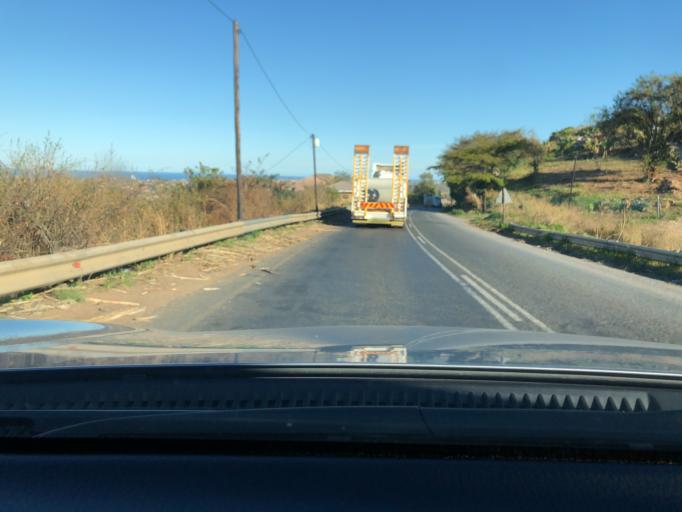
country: ZA
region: KwaZulu-Natal
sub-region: eThekwini Metropolitan Municipality
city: Umkomaas
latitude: -30.0226
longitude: 30.8113
